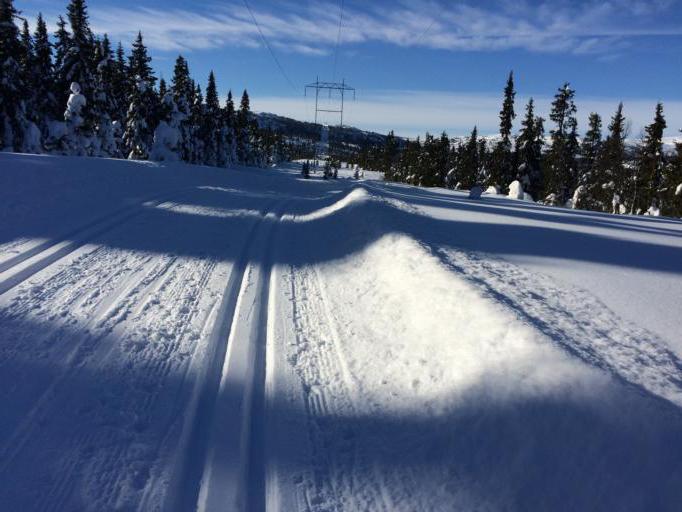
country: NO
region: Oppland
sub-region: Gausdal
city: Segalstad bru
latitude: 61.3196
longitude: 10.0893
